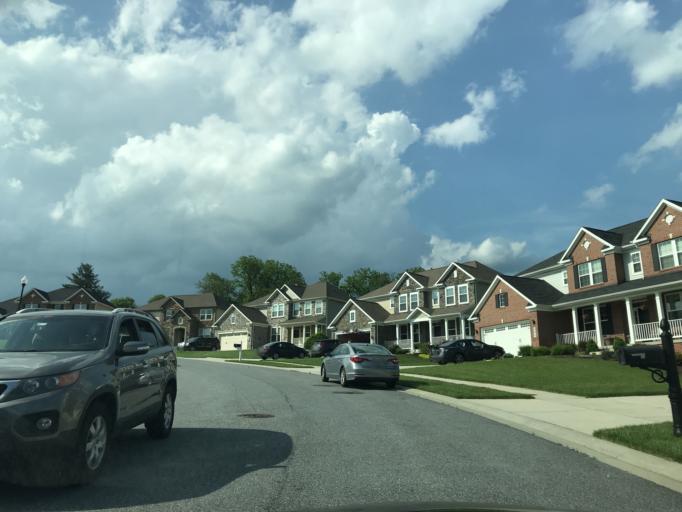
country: US
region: Maryland
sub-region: Harford County
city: Bel Air North
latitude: 39.5539
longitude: -76.3881
